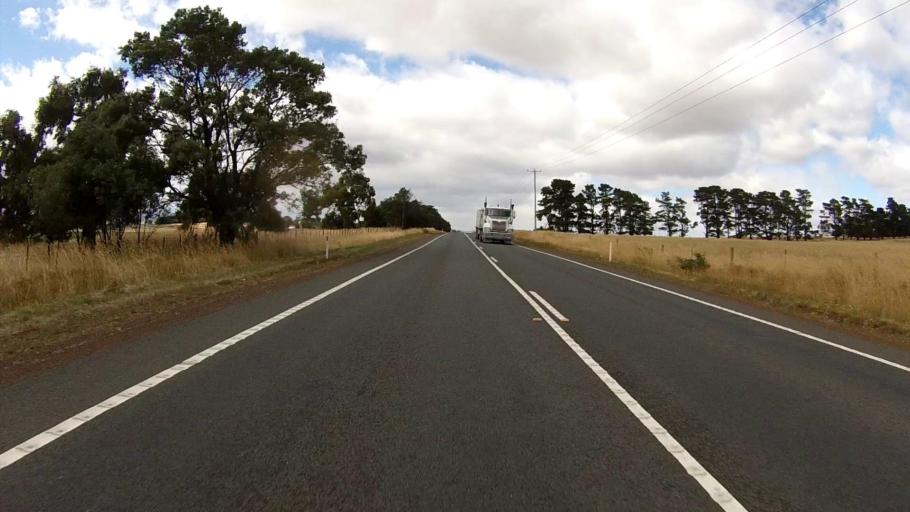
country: AU
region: Tasmania
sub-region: Northern Midlands
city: Evandale
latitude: -41.9090
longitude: 147.4807
